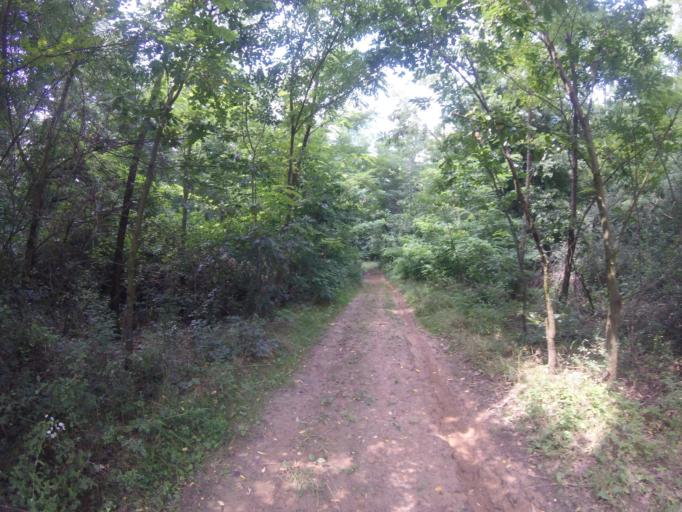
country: SK
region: Nitriansky
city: Sahy
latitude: 48.0242
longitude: 18.9477
